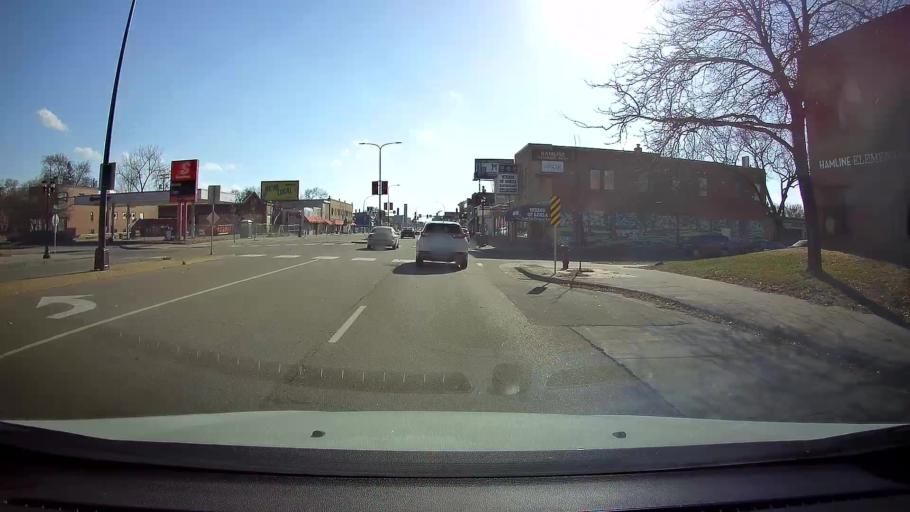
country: US
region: Minnesota
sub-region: Ramsey County
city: Falcon Heights
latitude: 44.9644
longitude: -93.1672
